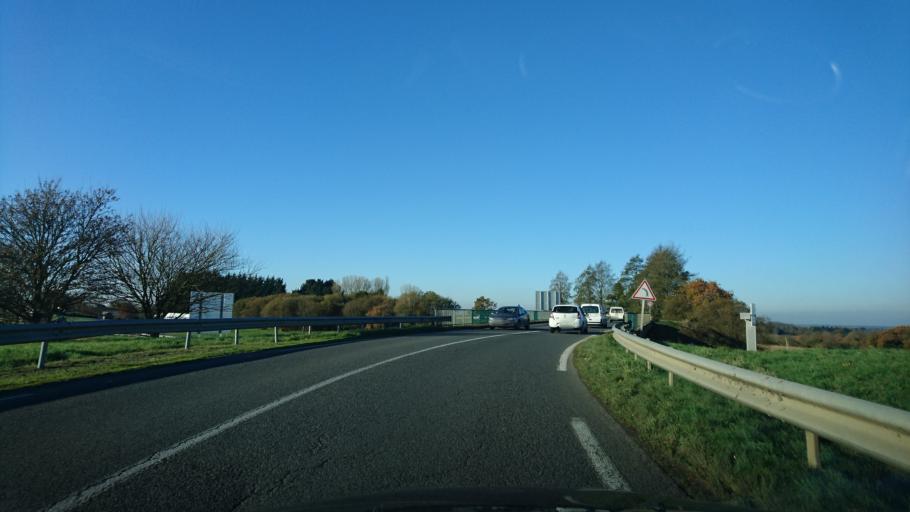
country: FR
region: Brittany
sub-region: Departement des Cotes-d'Armor
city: Tremuson
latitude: 48.5226
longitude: -2.8732
